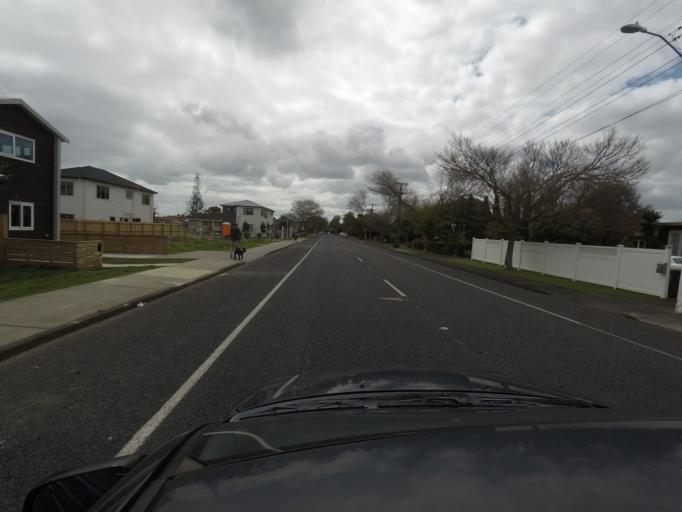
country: NZ
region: Auckland
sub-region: Auckland
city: Tamaki
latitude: -36.9377
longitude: 174.8574
